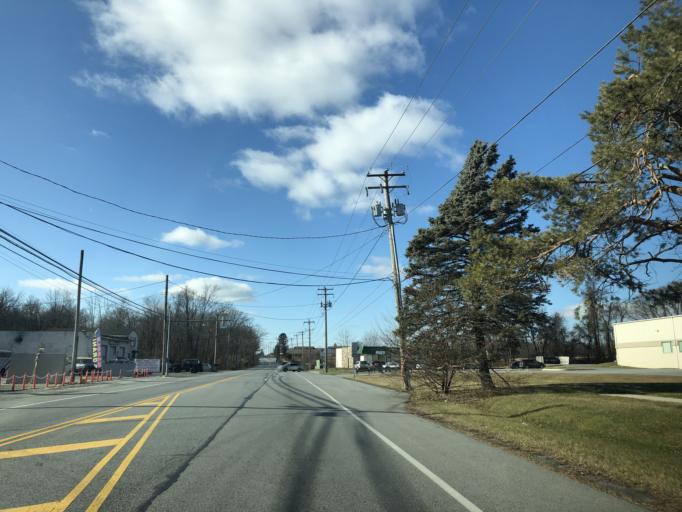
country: US
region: Pennsylvania
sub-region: Chester County
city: Coatesville
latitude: 39.9842
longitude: -75.8568
